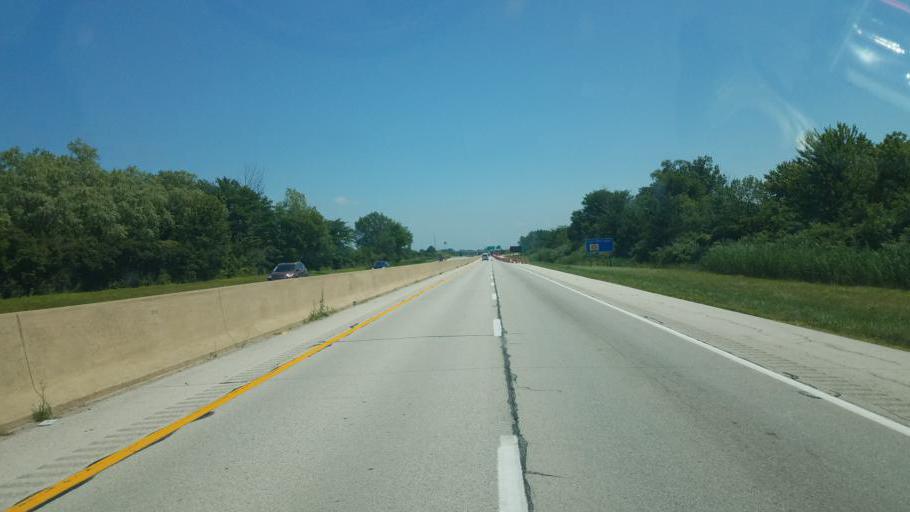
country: US
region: Ohio
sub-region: Ottawa County
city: Port Clinton
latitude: 41.5051
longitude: -82.9795
